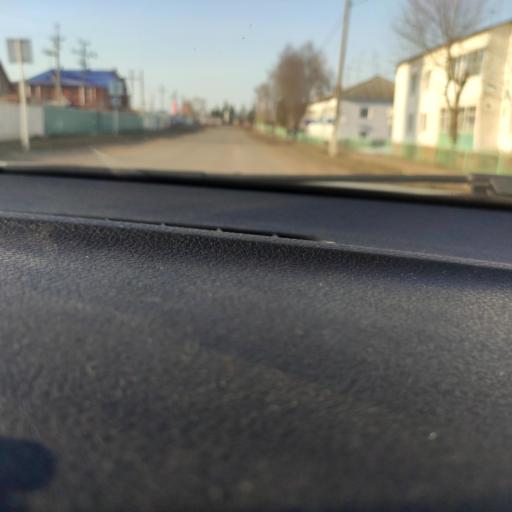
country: RU
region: Bashkortostan
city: Ulukulevo
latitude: 54.3772
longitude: 56.4496
